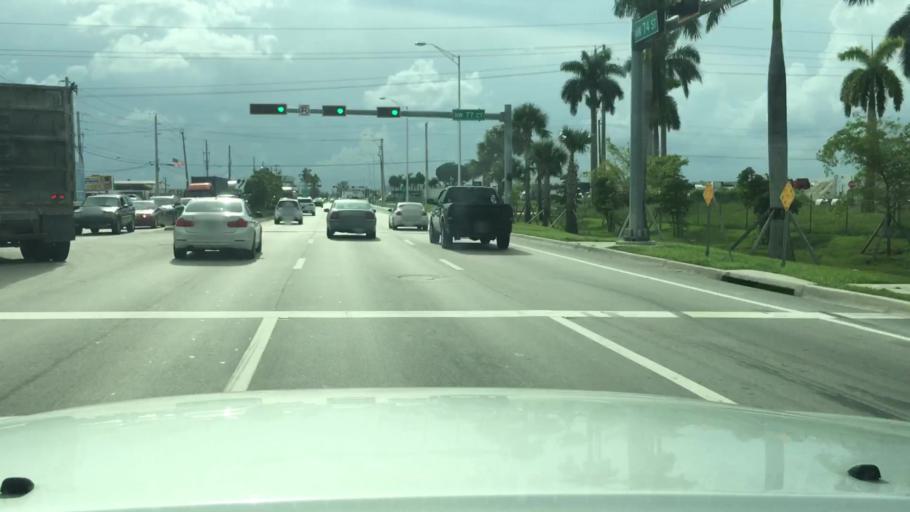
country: US
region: Florida
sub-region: Miami-Dade County
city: Hialeah Gardens
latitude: 25.8408
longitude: -80.3244
